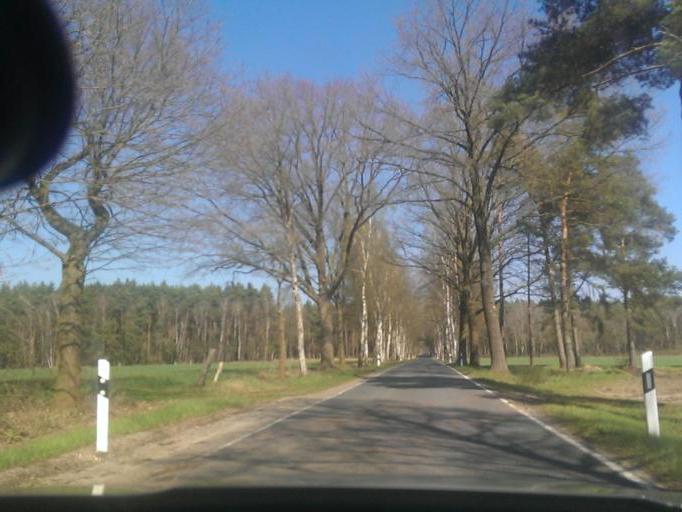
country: DE
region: Lower Saxony
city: Elze
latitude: 52.5288
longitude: 9.6961
